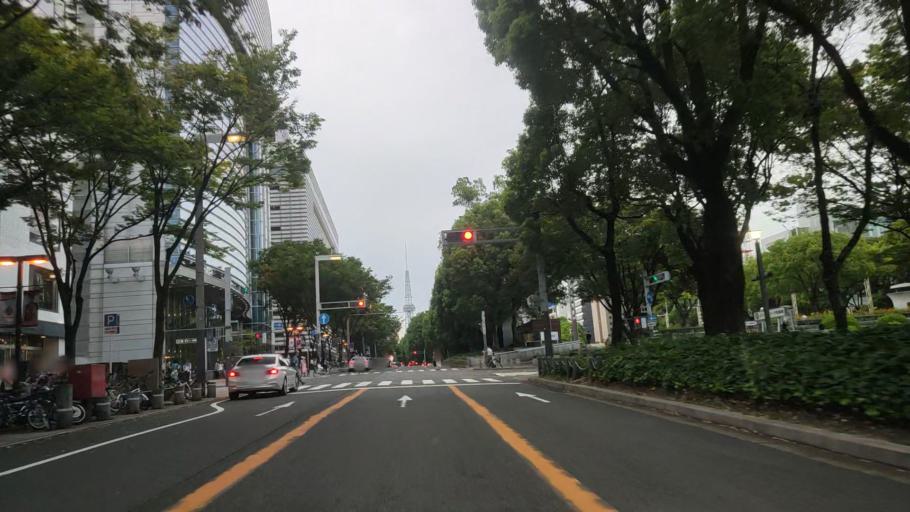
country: JP
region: Aichi
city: Nagoya-shi
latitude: 35.1638
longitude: 136.9086
